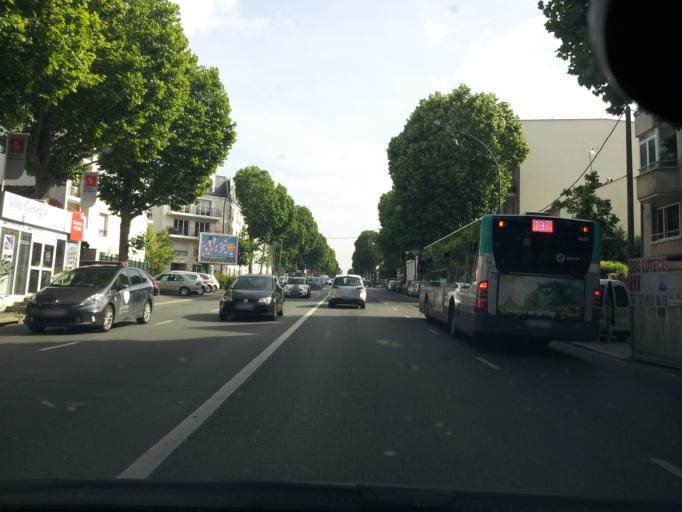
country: FR
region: Ile-de-France
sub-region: Departement des Hauts-de-Seine
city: Antony
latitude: 48.7459
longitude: 2.3032
